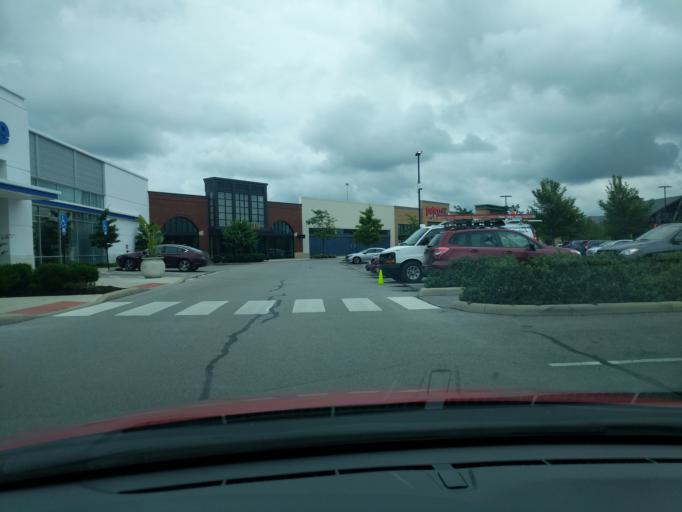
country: US
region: Ohio
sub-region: Franklin County
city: Huber Ridge
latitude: 40.0564
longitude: -82.9073
